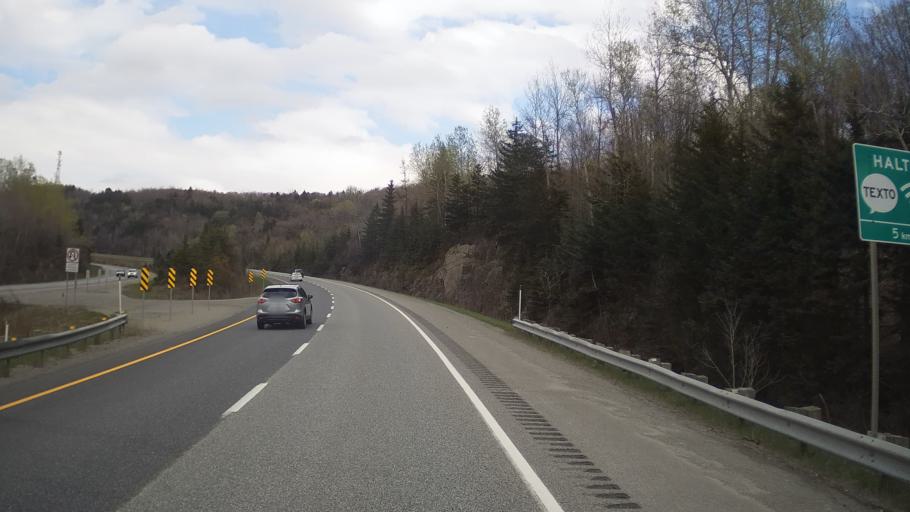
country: CA
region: Quebec
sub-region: Estrie
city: Magog
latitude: 45.2856
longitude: -72.2792
